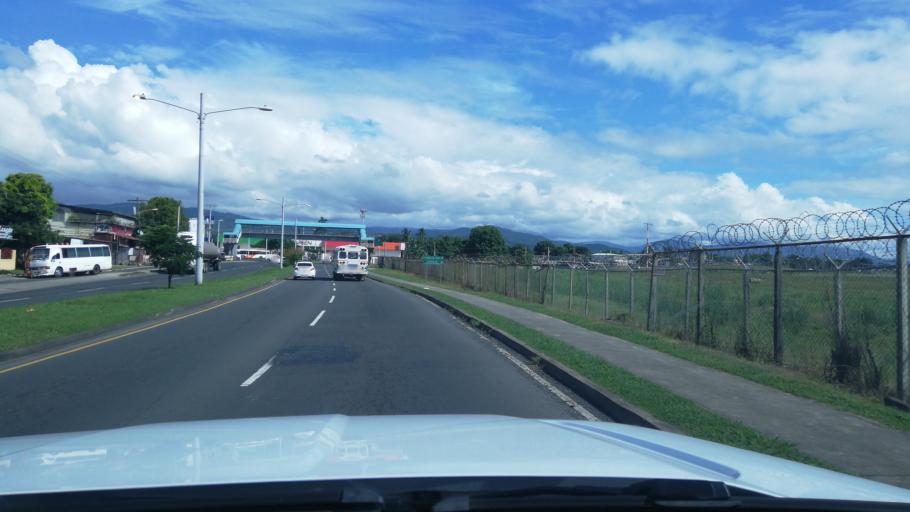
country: PA
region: Panama
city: Tocumen
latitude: 9.0849
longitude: -79.3841
